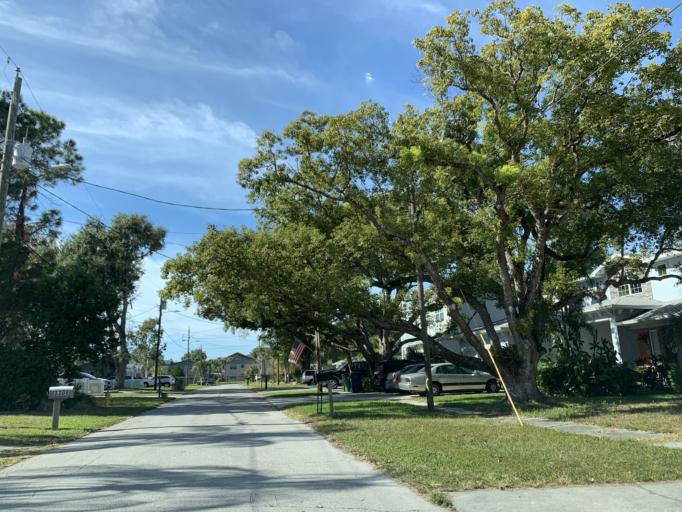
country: US
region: Florida
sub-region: Hillsborough County
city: Tampa
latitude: 27.8918
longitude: -82.4986
